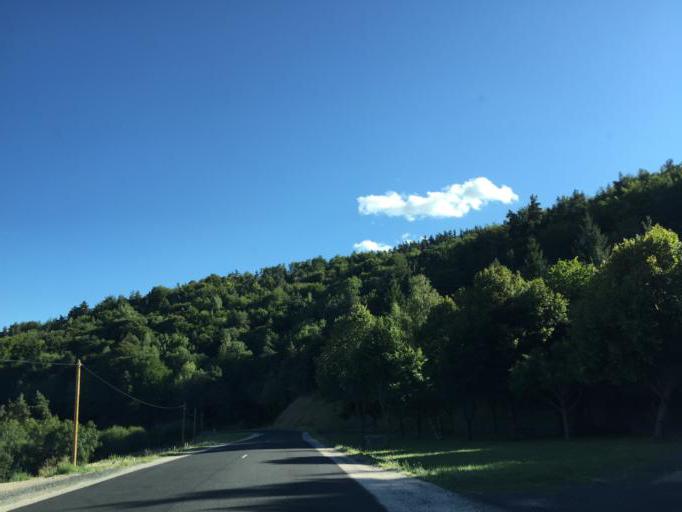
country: FR
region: Auvergne
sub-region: Departement de la Haute-Loire
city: Saugues
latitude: 44.9771
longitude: 3.6270
